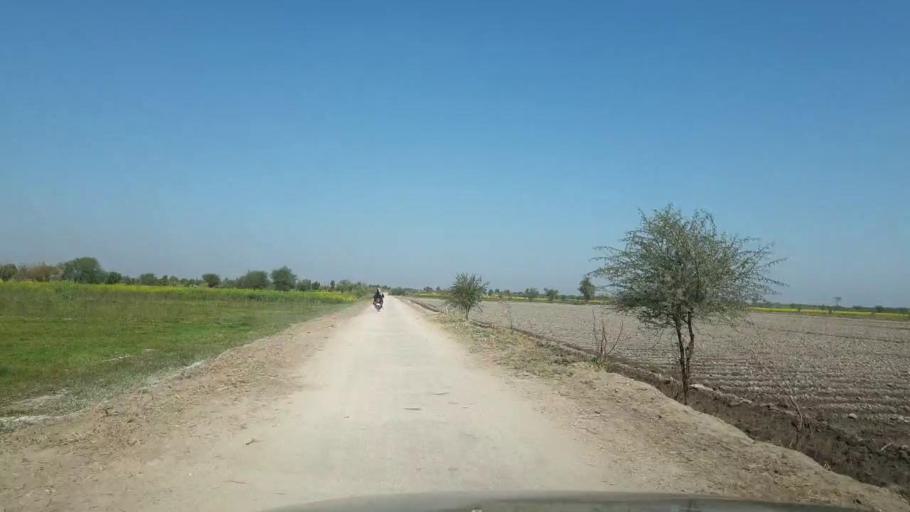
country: PK
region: Sindh
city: Mirpur Khas
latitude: 25.5910
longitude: 69.0684
